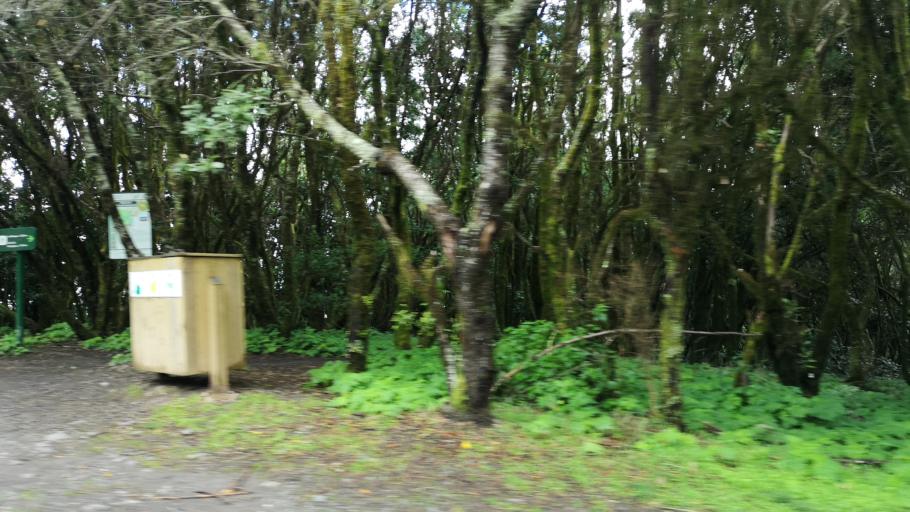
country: ES
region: Canary Islands
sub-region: Provincia de Santa Cruz de Tenerife
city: Alajero
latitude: 28.1122
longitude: -17.2180
